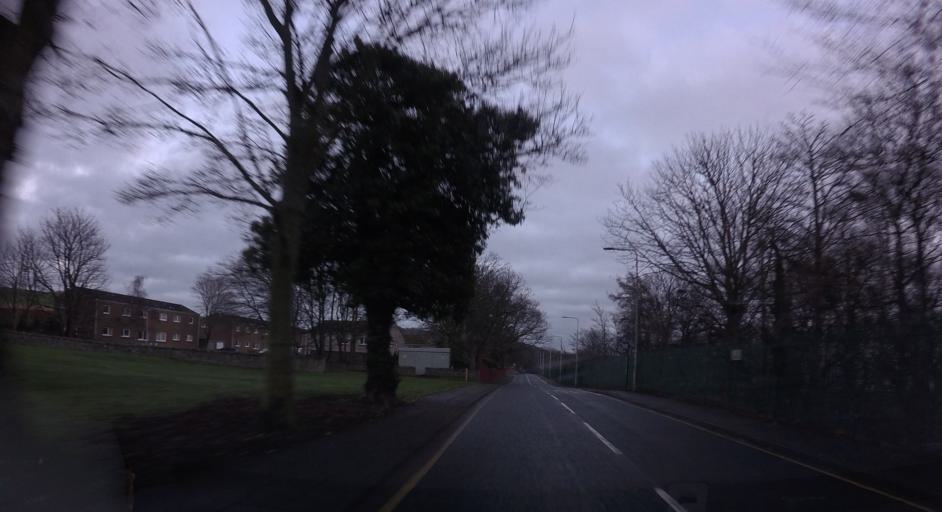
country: GB
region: Scotland
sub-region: Fife
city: Rosyth
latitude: 56.0261
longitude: -3.4253
